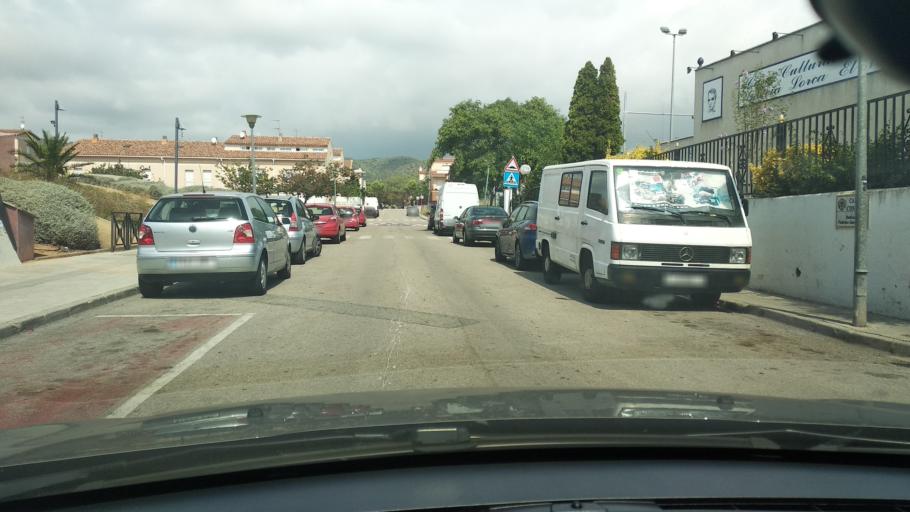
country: ES
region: Catalonia
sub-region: Provincia de Tarragona
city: El Vendrell
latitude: 41.2214
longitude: 1.5237
